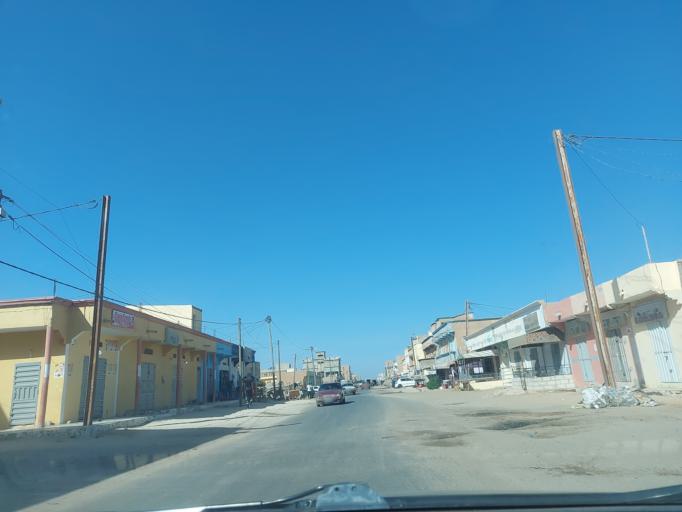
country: MR
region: Nouakchott
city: Nouakchott
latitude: 18.0661
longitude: -15.9979
